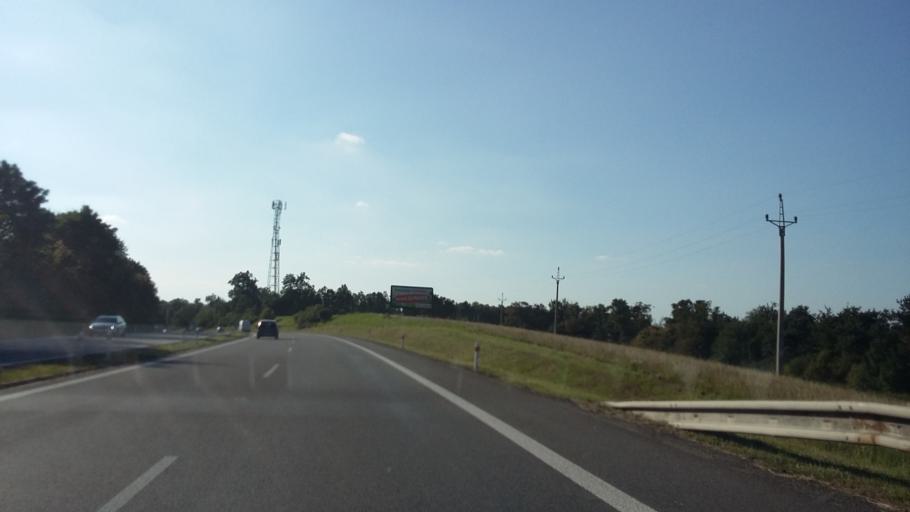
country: CZ
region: South Moravian
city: Ricany
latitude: 49.1921
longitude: 16.4341
